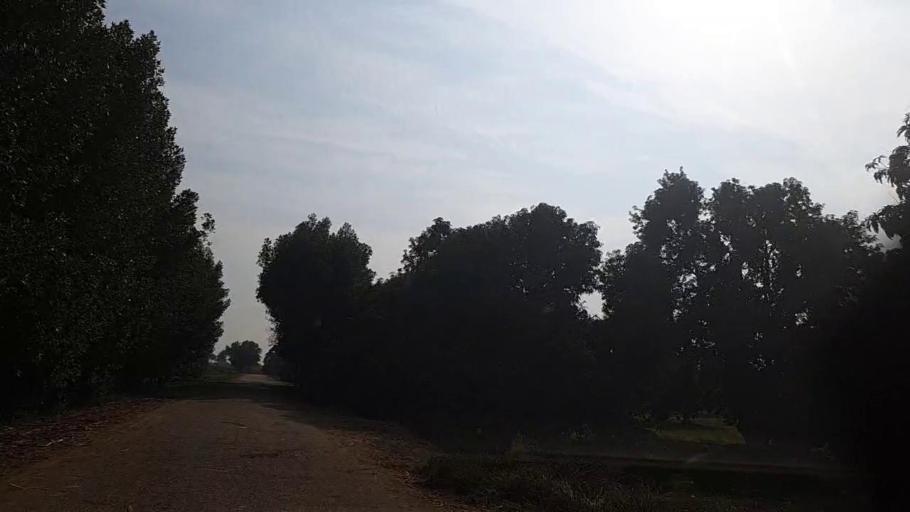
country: PK
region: Sindh
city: Daur
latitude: 26.4011
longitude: 68.2133
